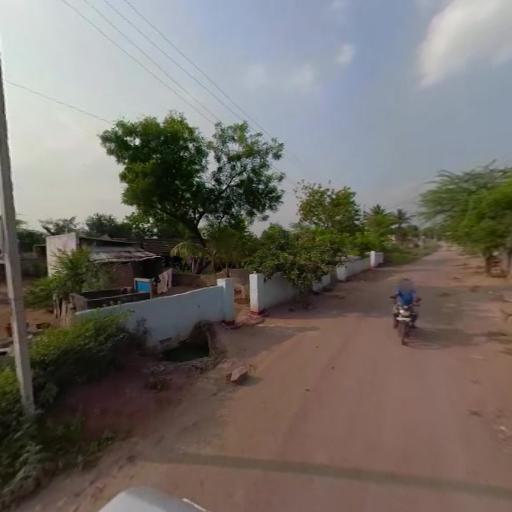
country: IN
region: Telangana
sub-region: Nalgonda
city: Suriapet
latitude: 17.1672
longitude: 79.5070
